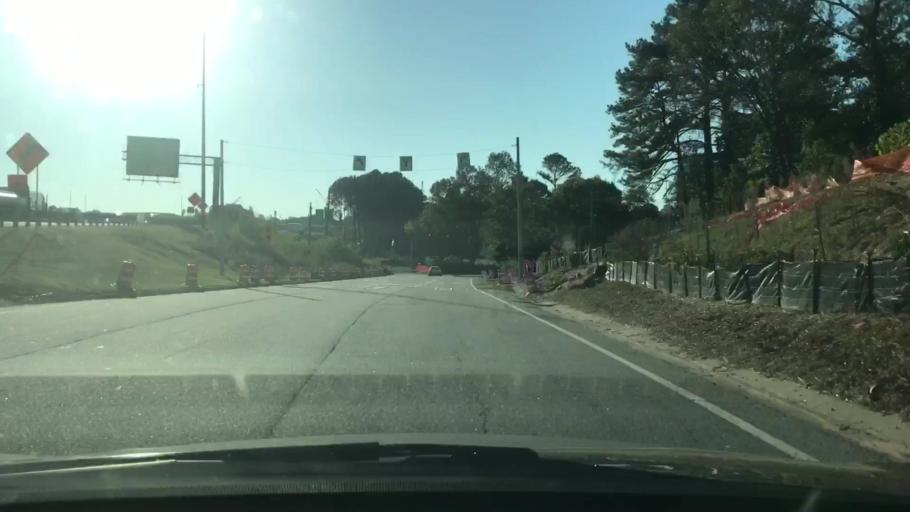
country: US
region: Georgia
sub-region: Fulton County
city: Sandy Springs
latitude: 33.9148
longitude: -84.3502
